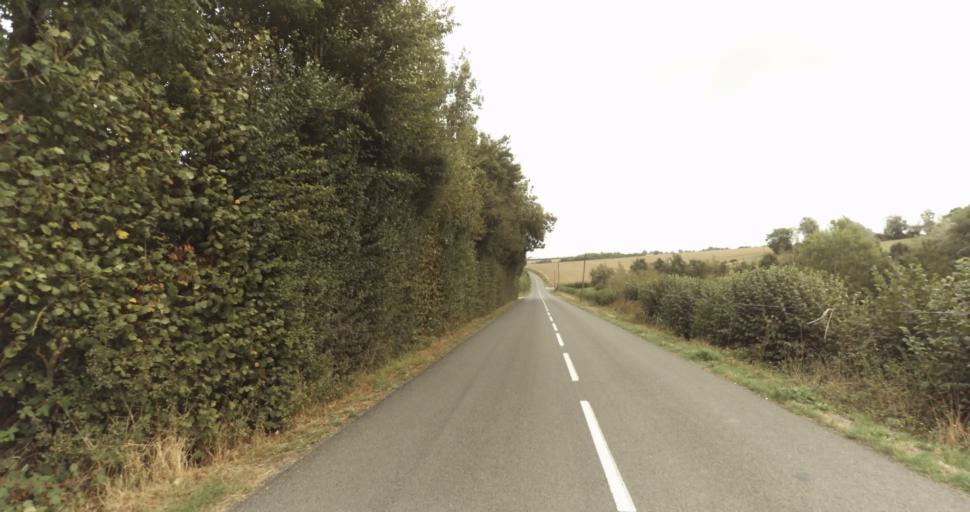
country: FR
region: Lower Normandy
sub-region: Departement de l'Orne
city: Gace
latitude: 48.8077
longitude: 0.3542
